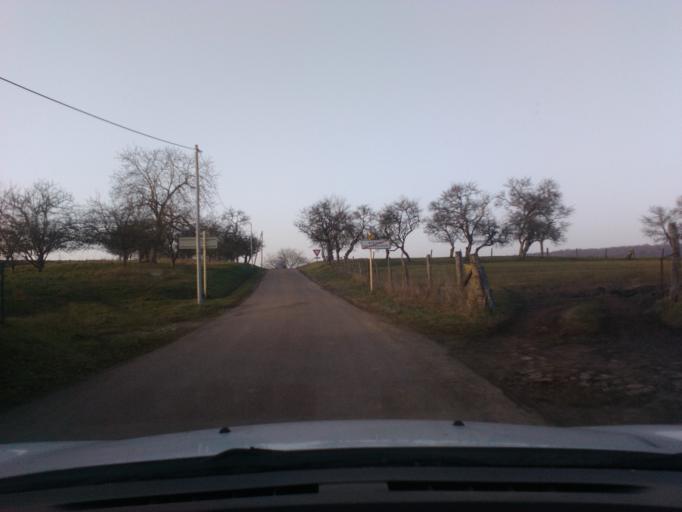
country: FR
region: Lorraine
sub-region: Departement des Vosges
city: Vittel
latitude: 48.2720
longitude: 6.0240
